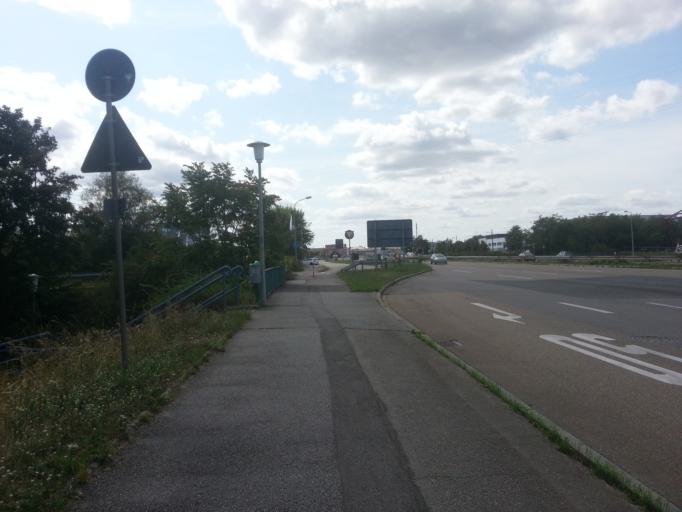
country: DE
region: Baden-Wuerttemberg
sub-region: Karlsruhe Region
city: Mannheim
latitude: 49.5099
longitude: 8.5251
